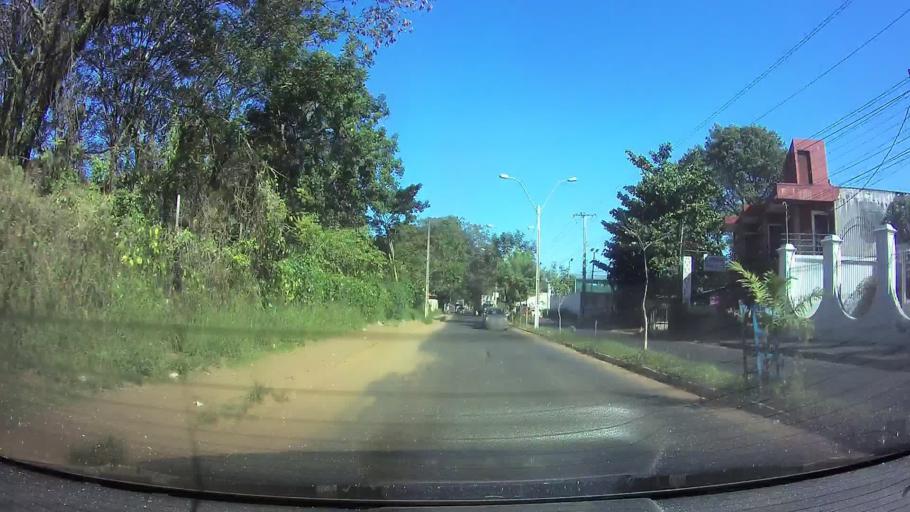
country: PY
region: Central
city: Villa Elisa
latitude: -25.3584
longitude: -57.5723
